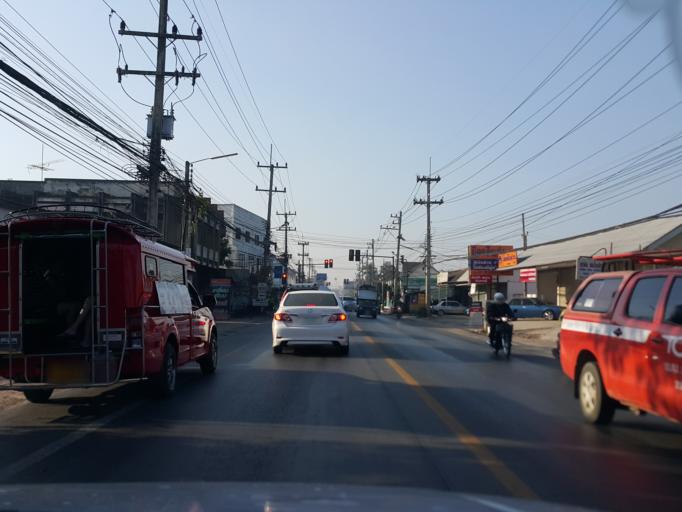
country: TH
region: Chiang Mai
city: San Pa Tong
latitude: 18.6328
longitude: 98.8978
